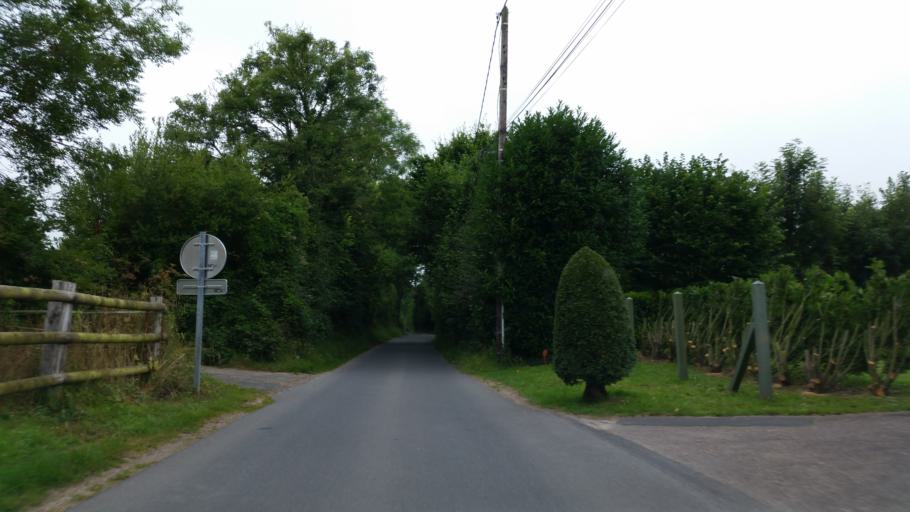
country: FR
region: Lower Normandy
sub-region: Departement du Calvados
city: Equemauville
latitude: 49.3920
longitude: 0.2326
